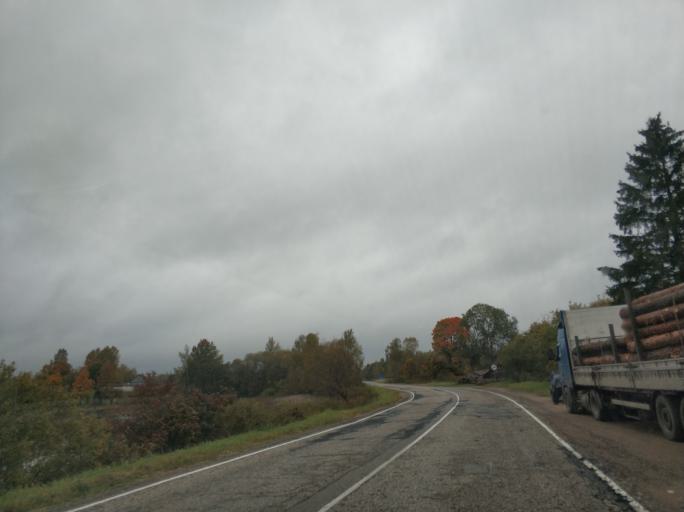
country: RU
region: Pskov
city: Sebezh
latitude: 56.2905
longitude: 28.5846
